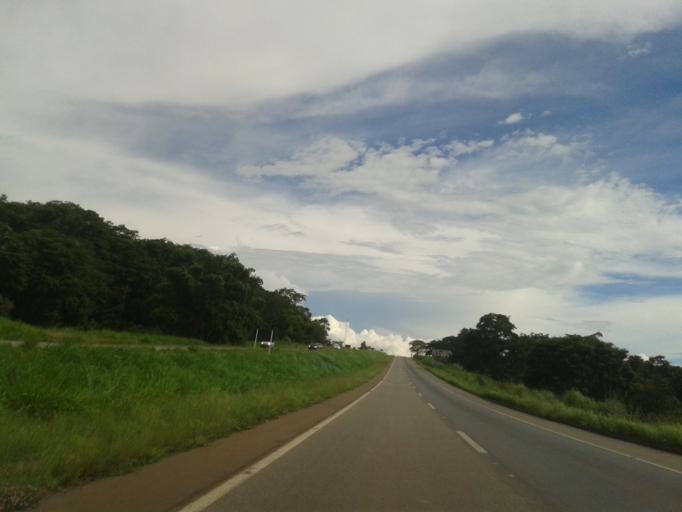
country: BR
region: Goias
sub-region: Hidrolandia
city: Hidrolandia
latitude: -16.9838
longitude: -49.2297
